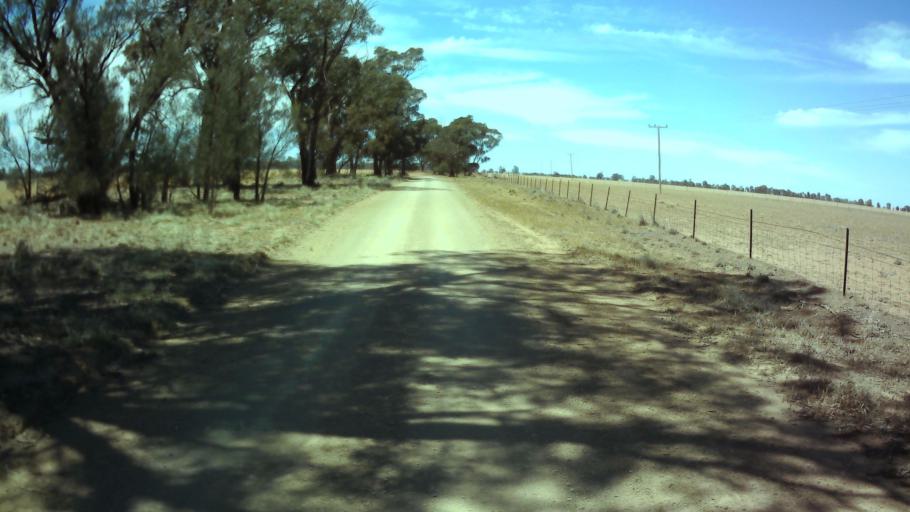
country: AU
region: New South Wales
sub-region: Weddin
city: Grenfell
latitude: -33.8888
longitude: 147.8032
